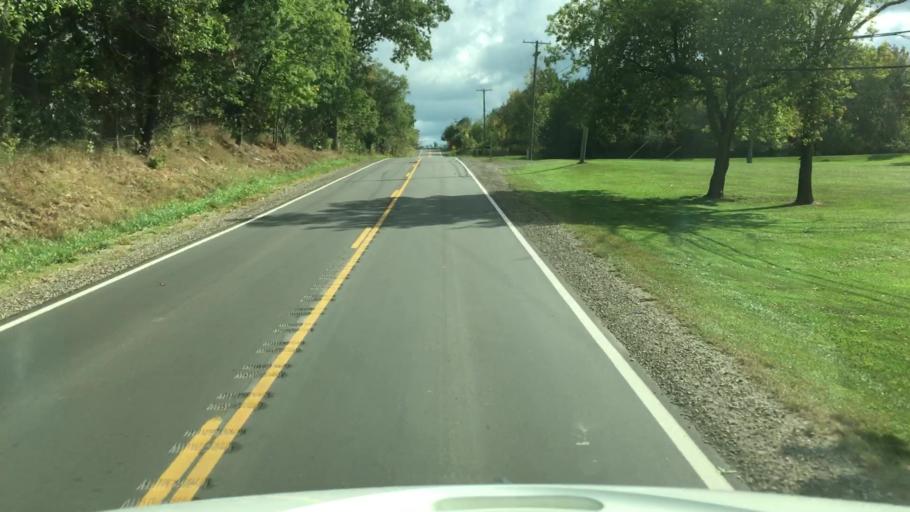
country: US
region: Michigan
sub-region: Oakland County
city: Oxford
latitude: 42.8681
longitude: -83.3254
